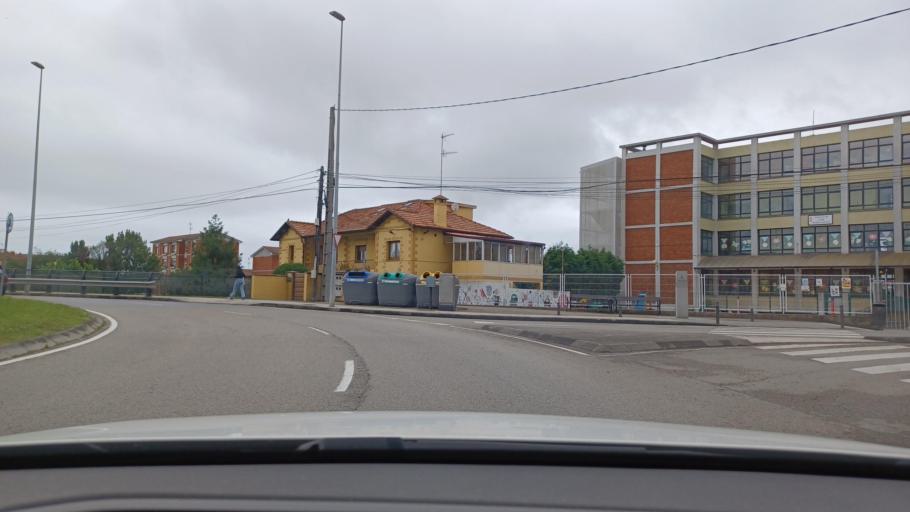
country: ES
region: Asturias
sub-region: Province of Asturias
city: Gijon
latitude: 43.5270
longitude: -5.6549
